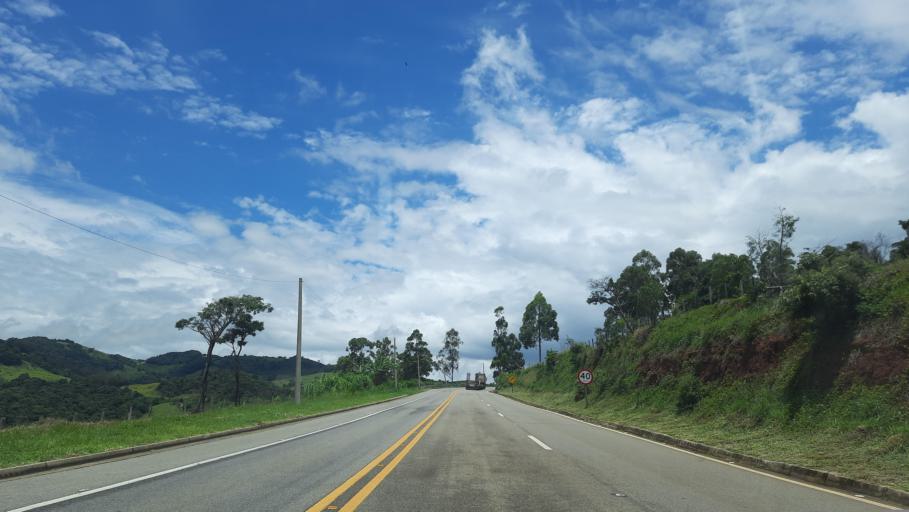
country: BR
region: Sao Paulo
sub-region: Vargem Grande Do Sul
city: Vargem Grande do Sul
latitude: -21.8288
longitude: -46.7685
